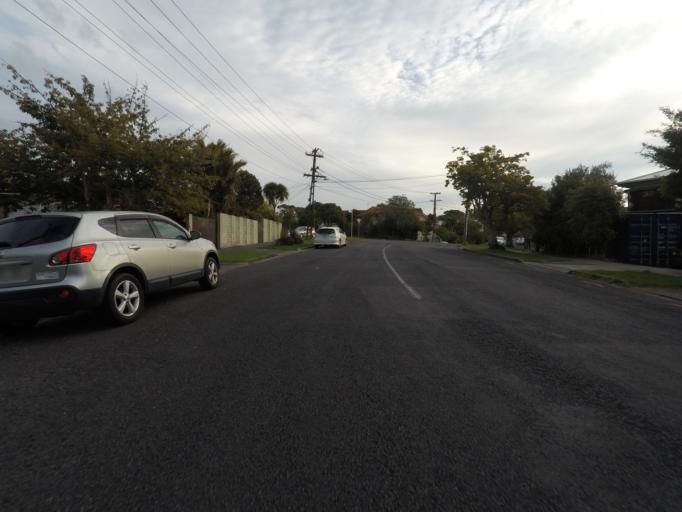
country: NZ
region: Auckland
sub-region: Auckland
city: Rosebank
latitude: -36.8797
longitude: 174.7169
